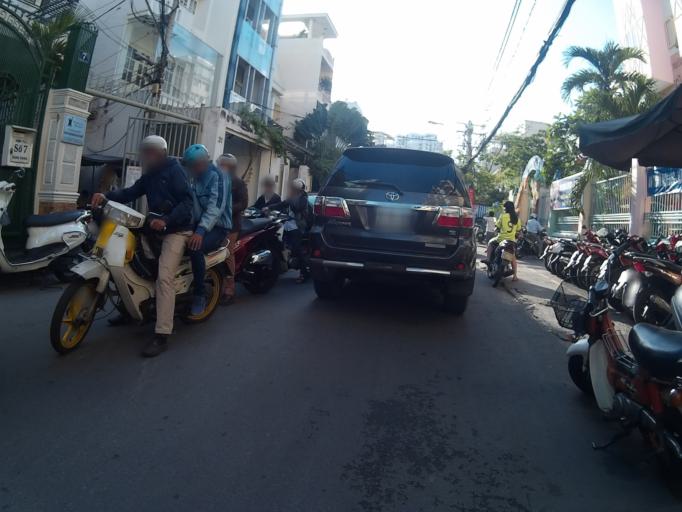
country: VN
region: Ho Chi Minh City
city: Quan Binh Thanh
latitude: 10.7927
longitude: 106.6909
